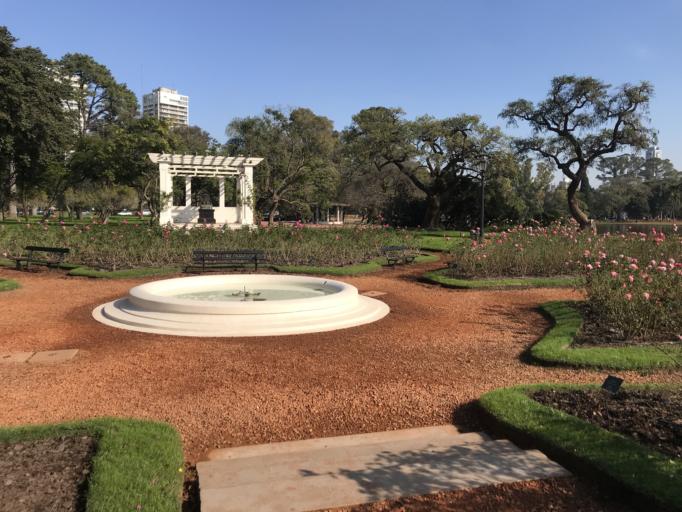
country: AR
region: Buenos Aires F.D.
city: Colegiales
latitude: -34.5708
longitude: -58.4175
